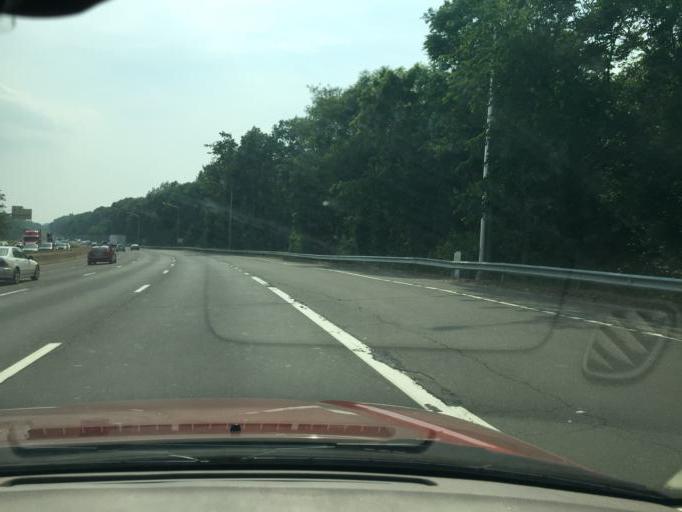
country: US
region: Connecticut
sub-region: Fairfield County
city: East Norwalk
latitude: 41.1201
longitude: -73.3782
